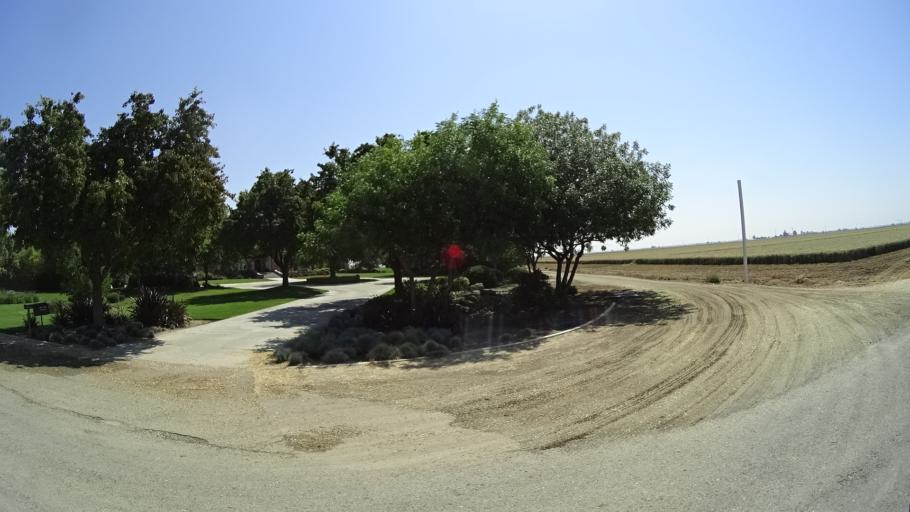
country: US
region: California
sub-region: Tulare County
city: Goshen
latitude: 36.3870
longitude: -119.5289
